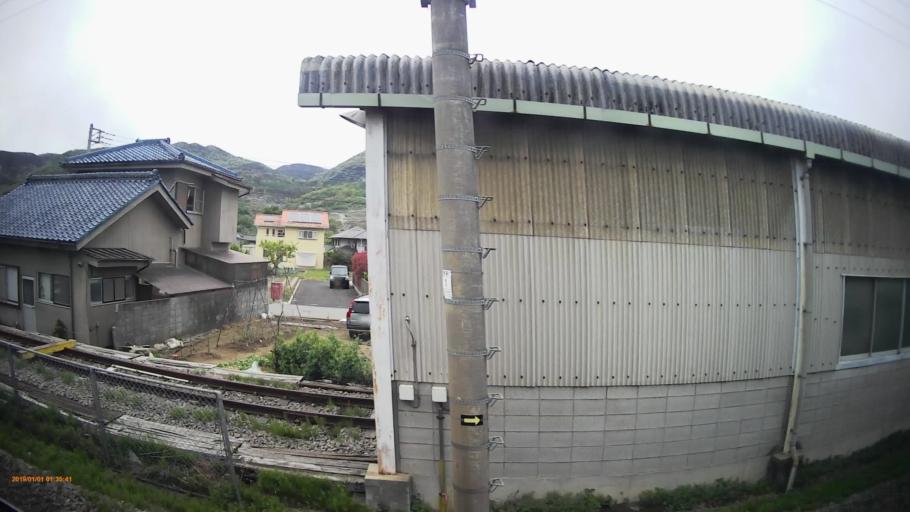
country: JP
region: Yamanashi
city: Isawa
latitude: 35.6743
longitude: 138.6599
